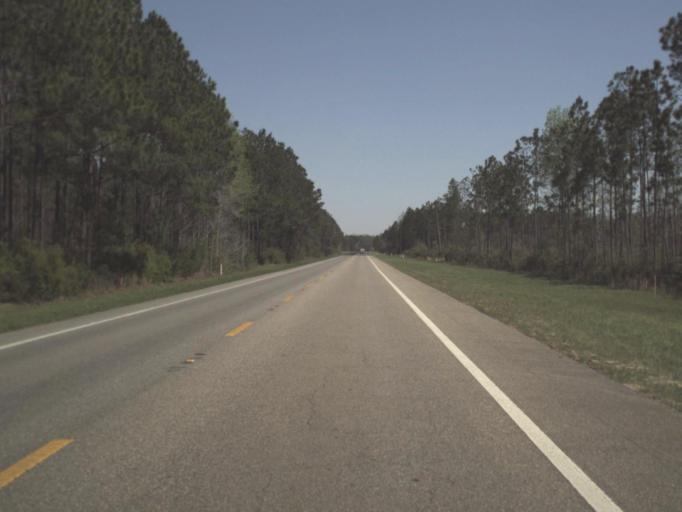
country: US
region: Florida
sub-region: Calhoun County
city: Blountstown
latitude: 30.4258
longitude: -85.1297
